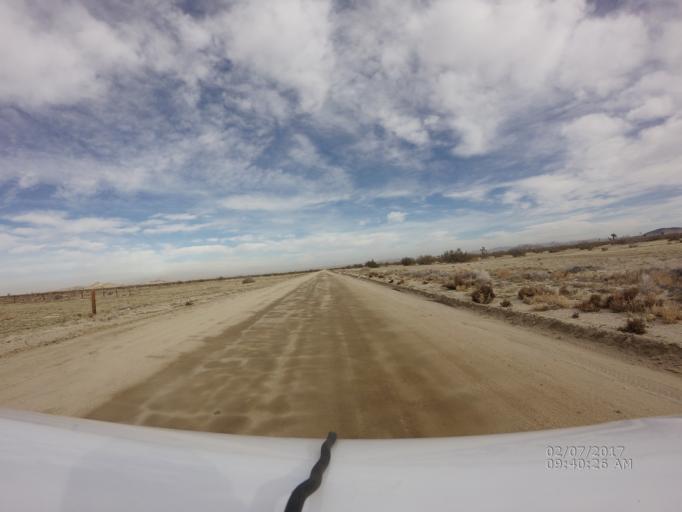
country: US
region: California
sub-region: Los Angeles County
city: Lake Los Angeles
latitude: 34.5605
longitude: -117.7114
